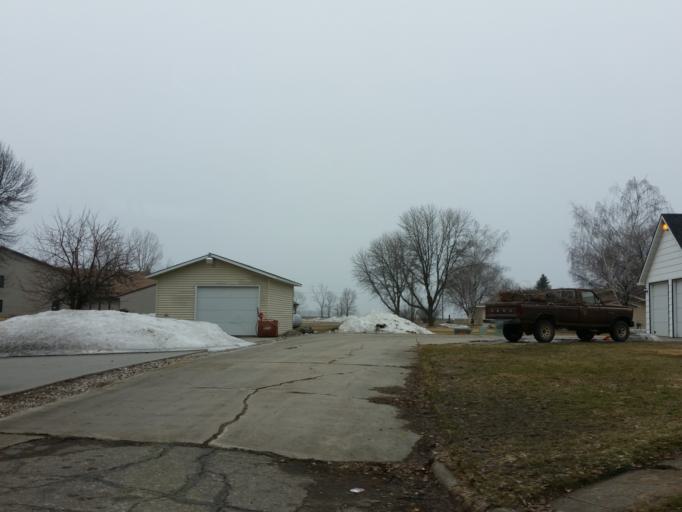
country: US
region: North Dakota
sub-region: Walsh County
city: Grafton
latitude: 48.5629
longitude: -97.1834
